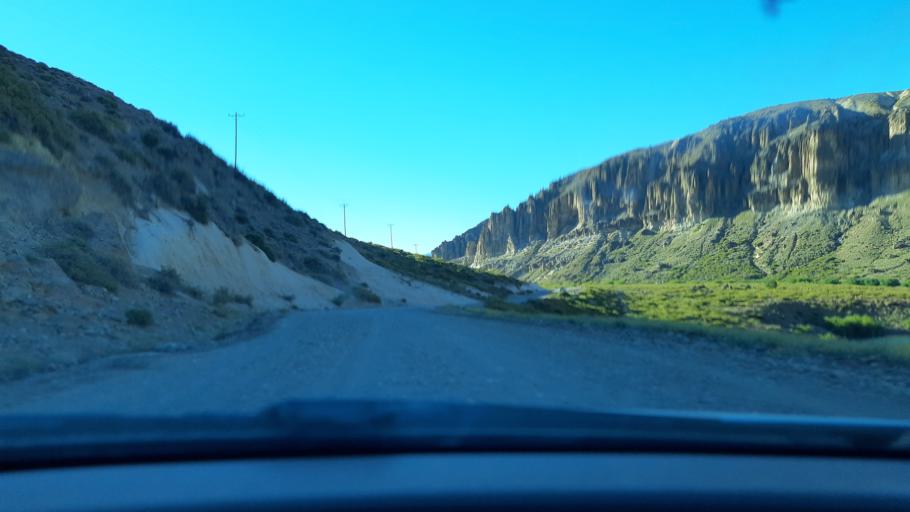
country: AR
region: Neuquen
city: Las Ovejas
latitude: -36.8051
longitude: -70.7239
